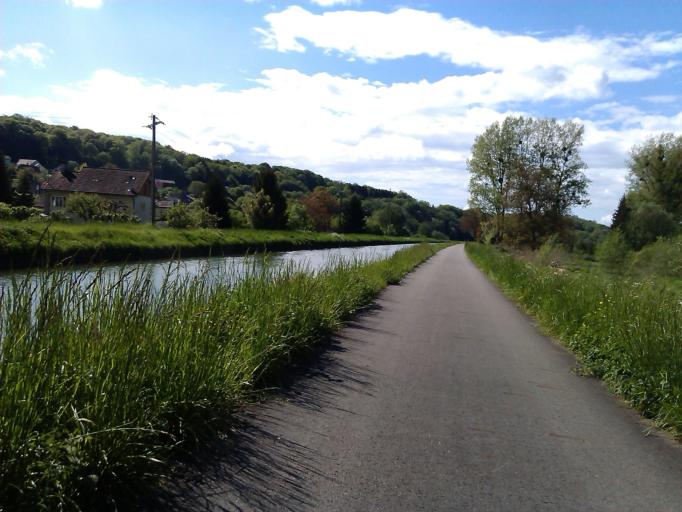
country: FR
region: Franche-Comte
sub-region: Departement du Doubs
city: Colombier-Fontaine
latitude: 47.4288
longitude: 6.6113
